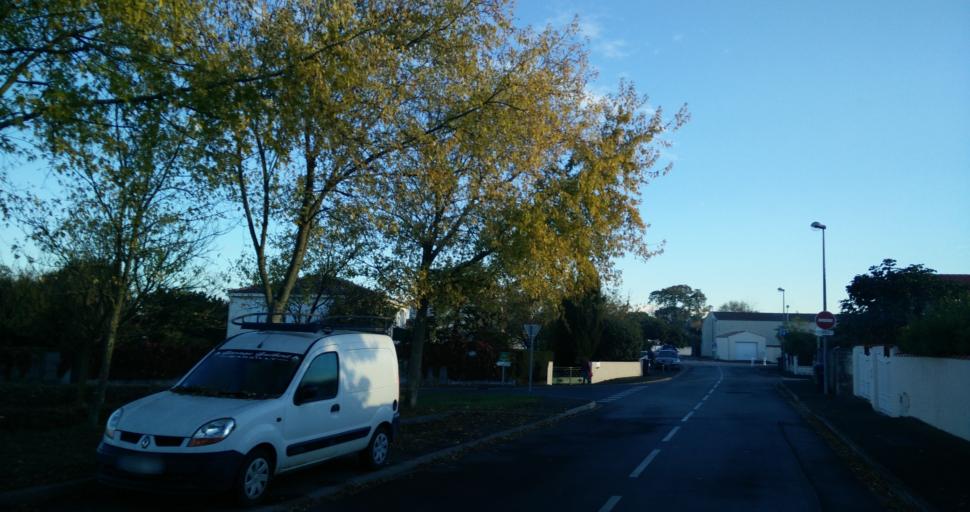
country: FR
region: Poitou-Charentes
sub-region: Departement de la Charente-Maritime
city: Puilboreau
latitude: 46.1858
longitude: -1.1211
